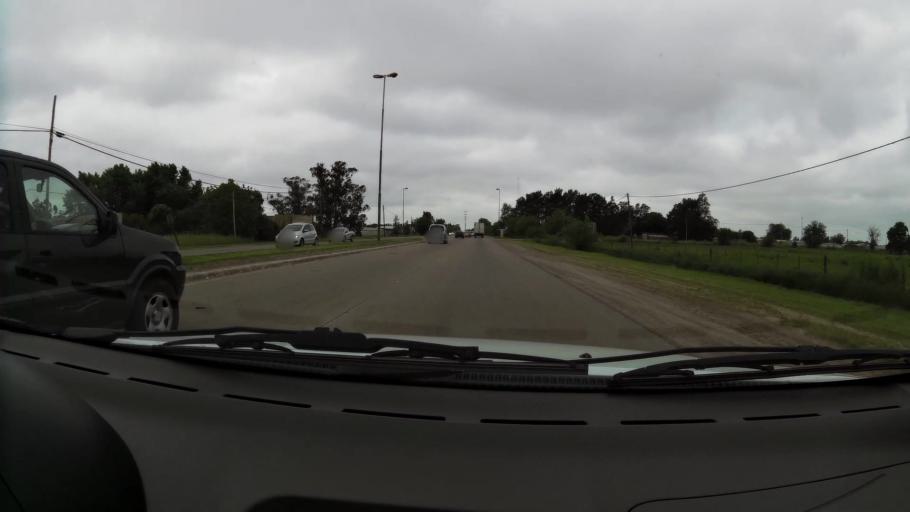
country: AR
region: Buenos Aires
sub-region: Partido de La Plata
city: La Plata
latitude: -35.0209
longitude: -58.0762
